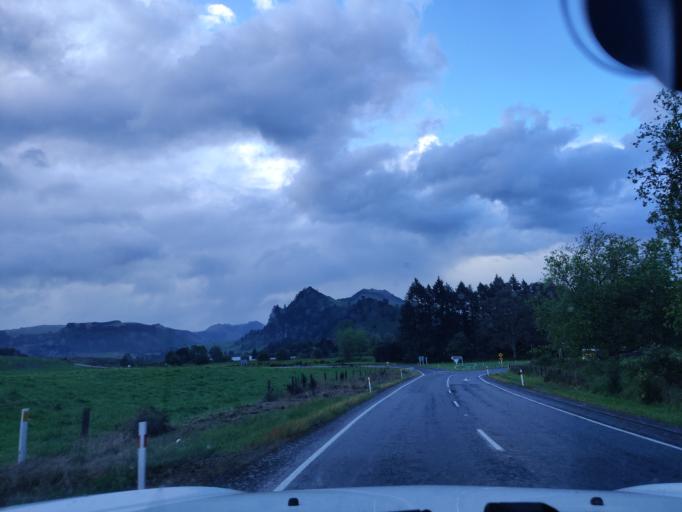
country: NZ
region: Waikato
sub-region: South Waikato District
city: Tokoroa
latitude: -38.4173
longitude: 175.8112
